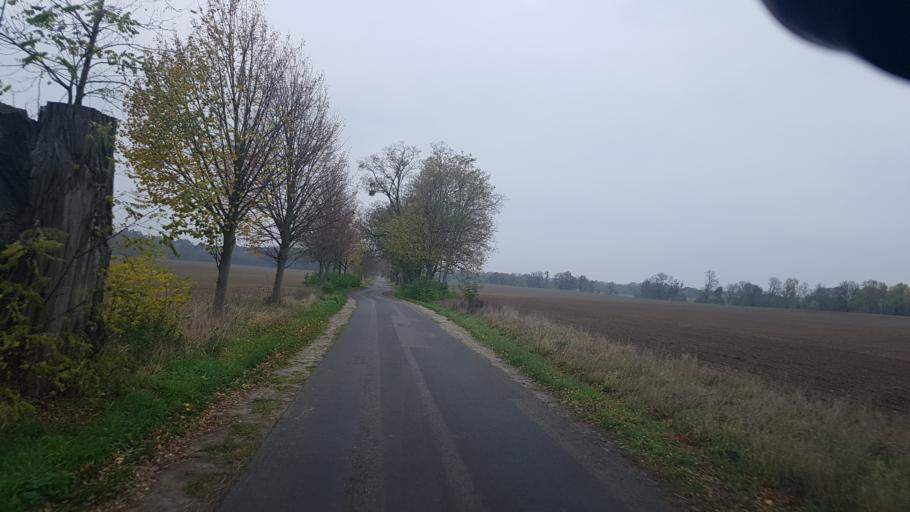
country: DE
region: Brandenburg
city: Lindow
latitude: 52.9401
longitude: 13.0613
